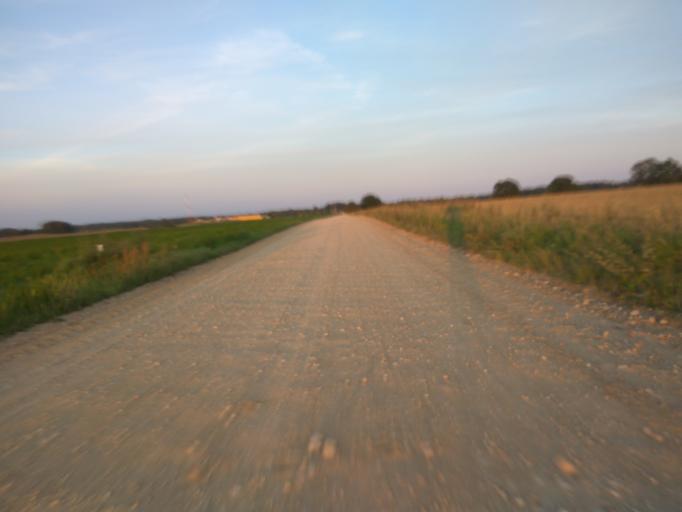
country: LV
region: Aizpute
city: Aizpute
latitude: 56.8378
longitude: 21.7435
